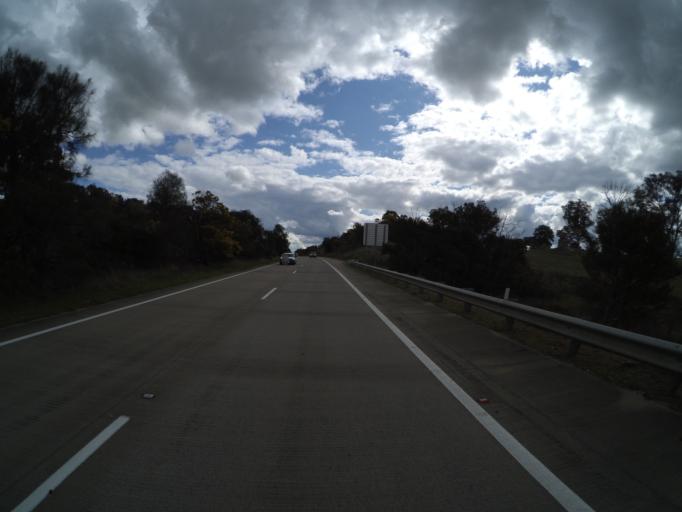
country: AU
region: New South Wales
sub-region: Yass Valley
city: Gundaroo
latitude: -34.7888
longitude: 149.2270
